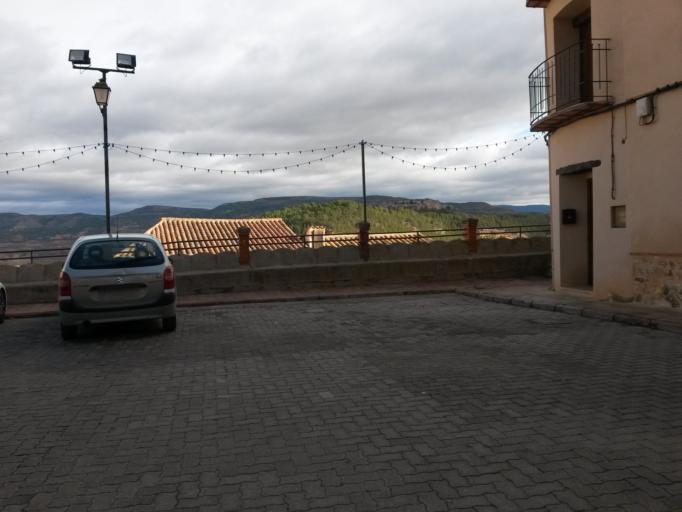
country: ES
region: Valencia
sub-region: Provincia de Valencia
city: Ademuz
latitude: 40.0613
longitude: -1.2865
